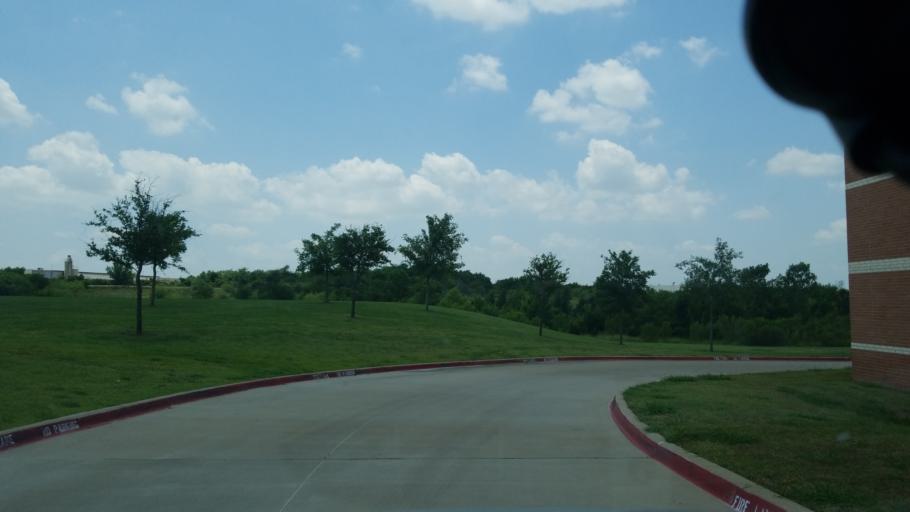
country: US
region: Texas
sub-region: Dallas County
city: Carrollton
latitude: 32.9641
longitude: -96.8796
